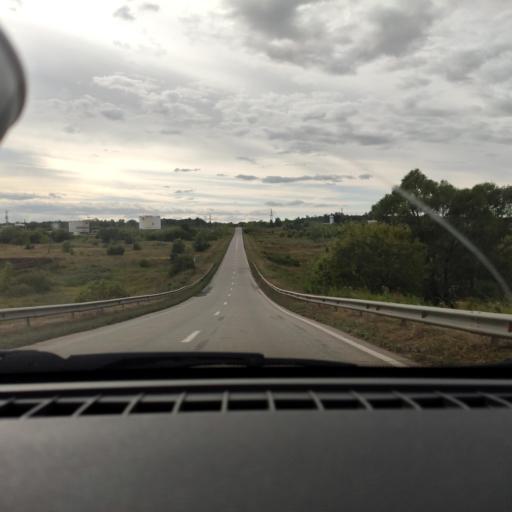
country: RU
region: Samara
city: Georgiyevka
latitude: 53.4195
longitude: 50.8535
